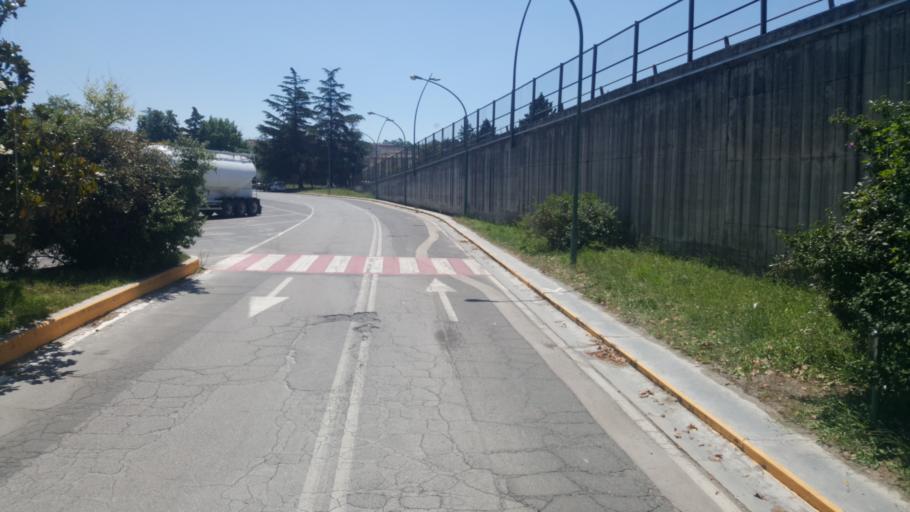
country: IT
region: Latium
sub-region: Citta metropolitana di Roma Capitale
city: Colleferro
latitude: 41.7362
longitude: 13.0072
